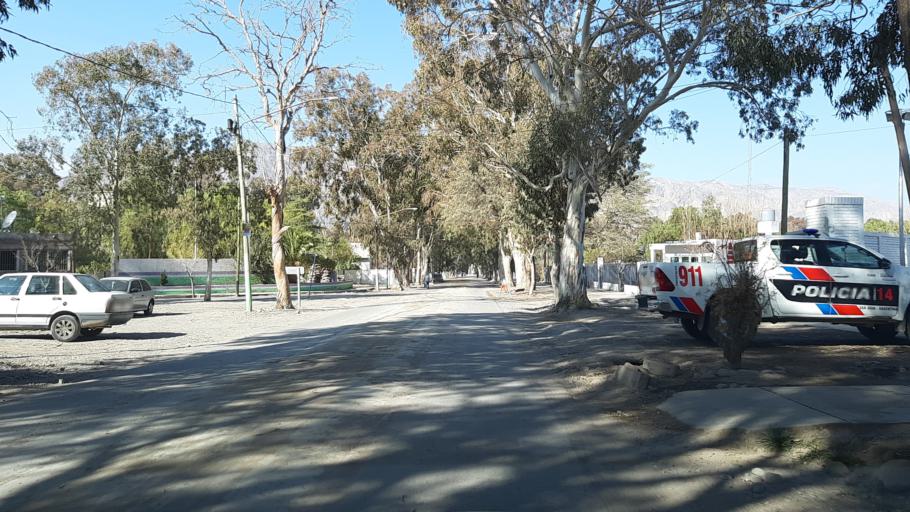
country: AR
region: San Juan
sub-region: Departamento de Zonda
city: Zonda
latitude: -31.5514
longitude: -68.7310
